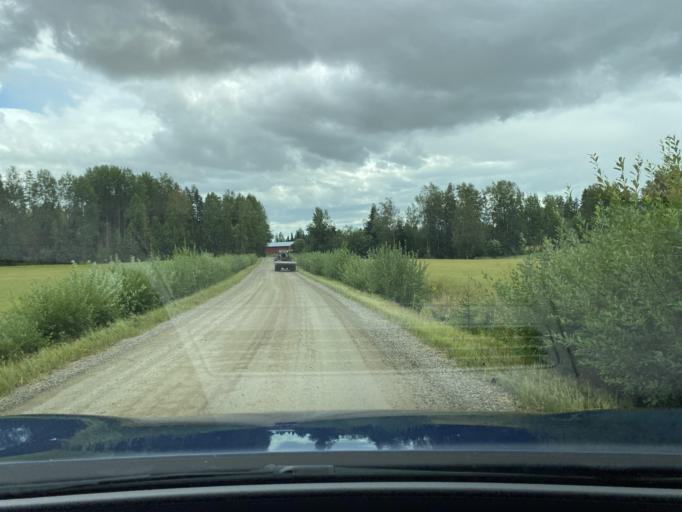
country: FI
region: Pirkanmaa
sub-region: Lounais-Pirkanmaa
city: Punkalaidun
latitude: 61.1735
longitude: 23.1801
